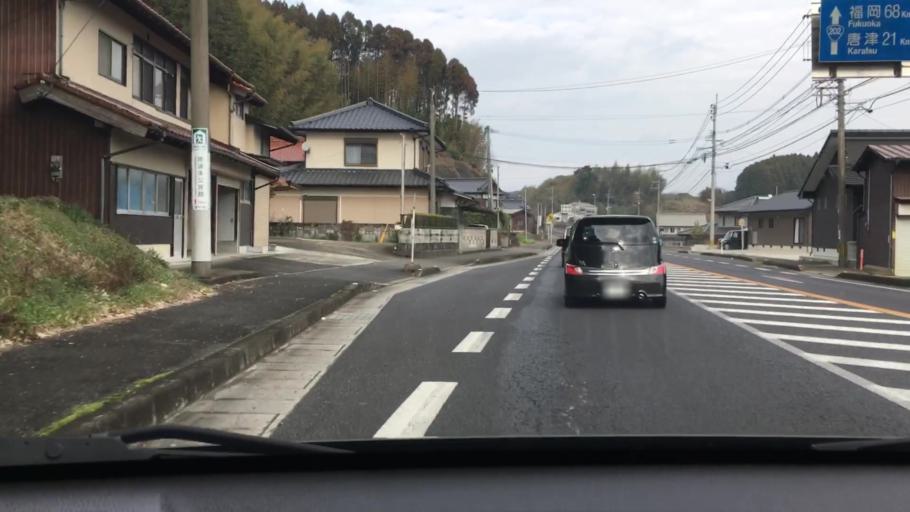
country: JP
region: Saga Prefecture
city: Imaricho-ko
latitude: 33.3071
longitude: 129.9263
